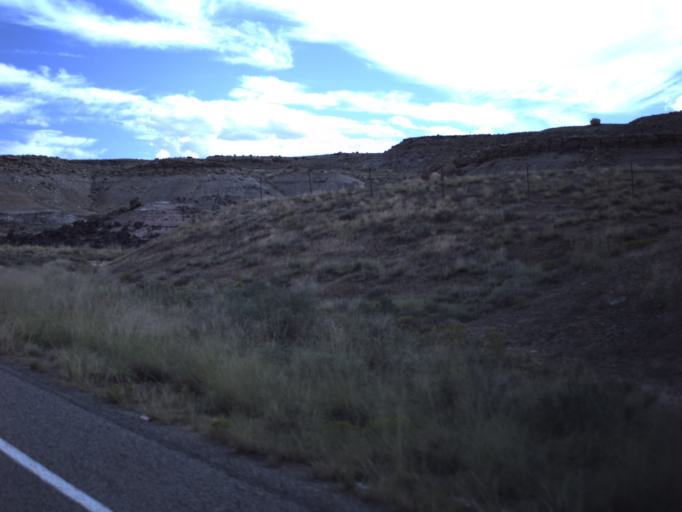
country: US
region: Colorado
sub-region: Montezuma County
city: Towaoc
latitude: 37.1525
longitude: -109.0484
